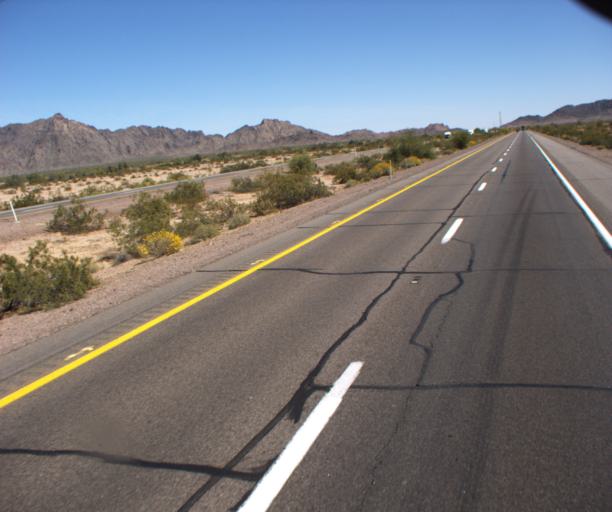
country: US
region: Arizona
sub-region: Yuma County
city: Wellton
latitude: 32.7176
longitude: -113.7934
